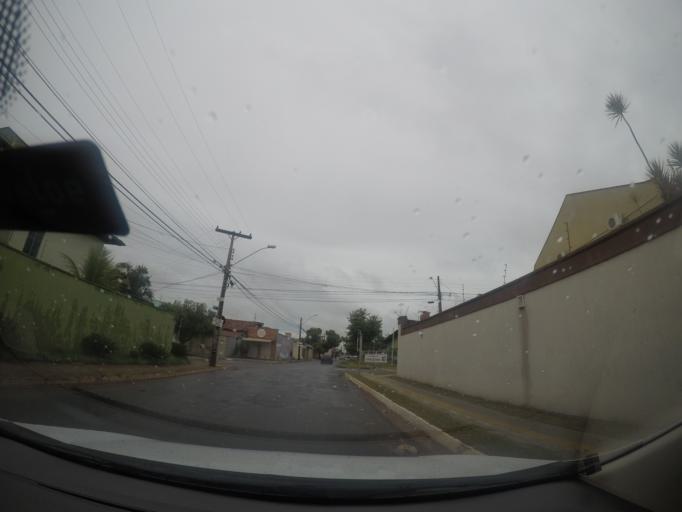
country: BR
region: Goias
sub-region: Goiania
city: Goiania
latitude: -16.7246
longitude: -49.3018
